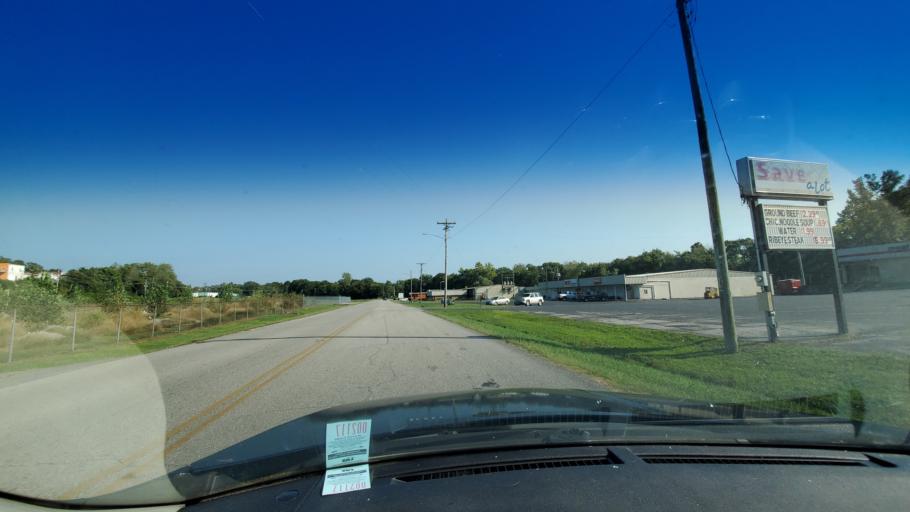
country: US
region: Tennessee
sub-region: Smith County
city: Carthage
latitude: 36.2633
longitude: -85.9580
